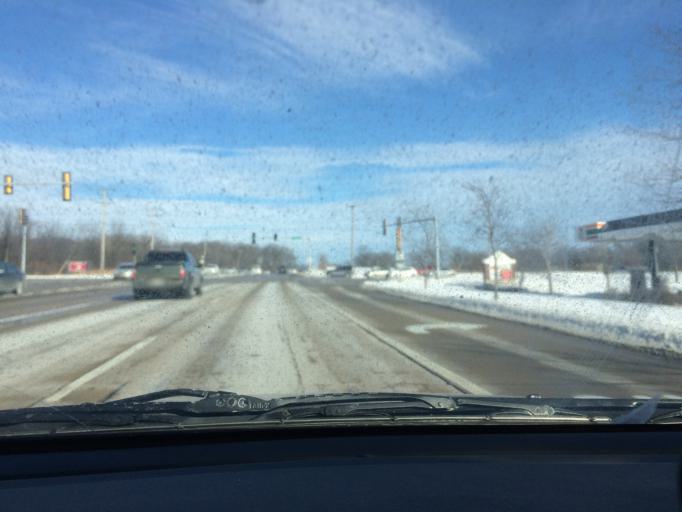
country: US
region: Illinois
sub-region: Cook County
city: Streamwood
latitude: 42.0308
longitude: -88.2020
